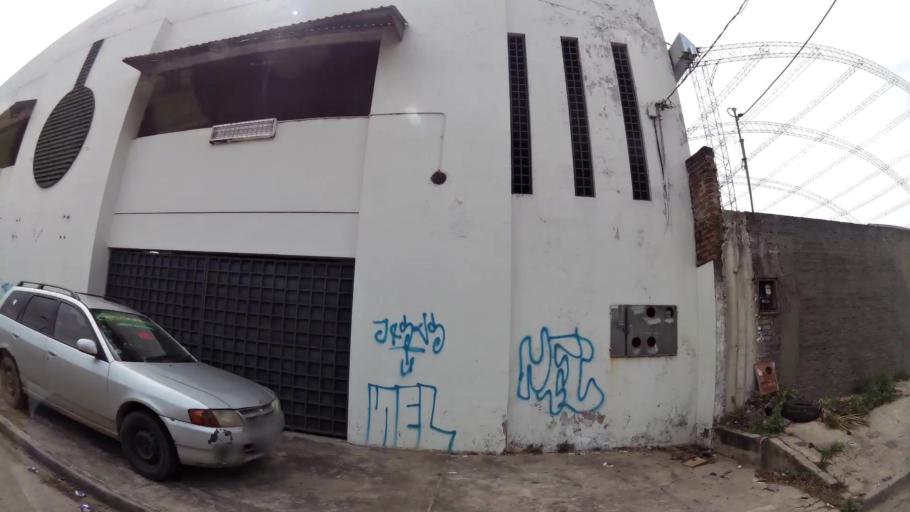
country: BO
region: Santa Cruz
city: Santa Cruz de la Sierra
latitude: -17.7845
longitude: -63.2007
